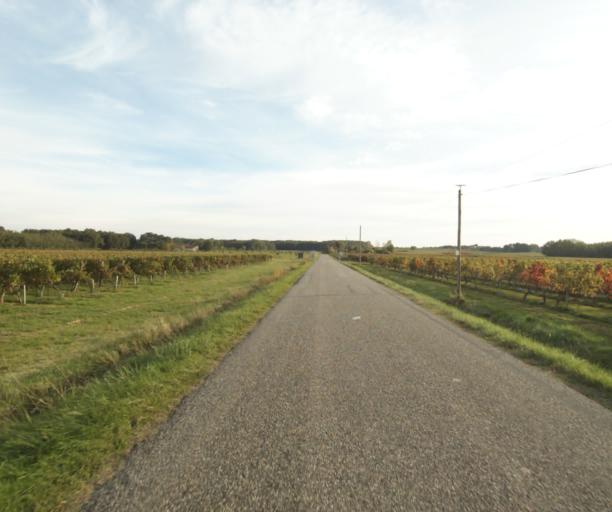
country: FR
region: Midi-Pyrenees
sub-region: Departement du Tarn-et-Garonne
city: Campsas
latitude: 43.8793
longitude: 1.3390
